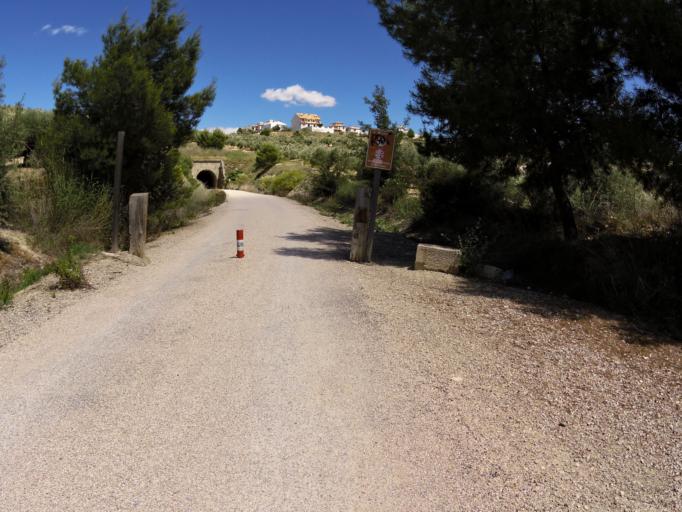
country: ES
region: Andalusia
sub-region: Provincia de Jaen
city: Torre del Campo
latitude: 37.7708
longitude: -3.9105
